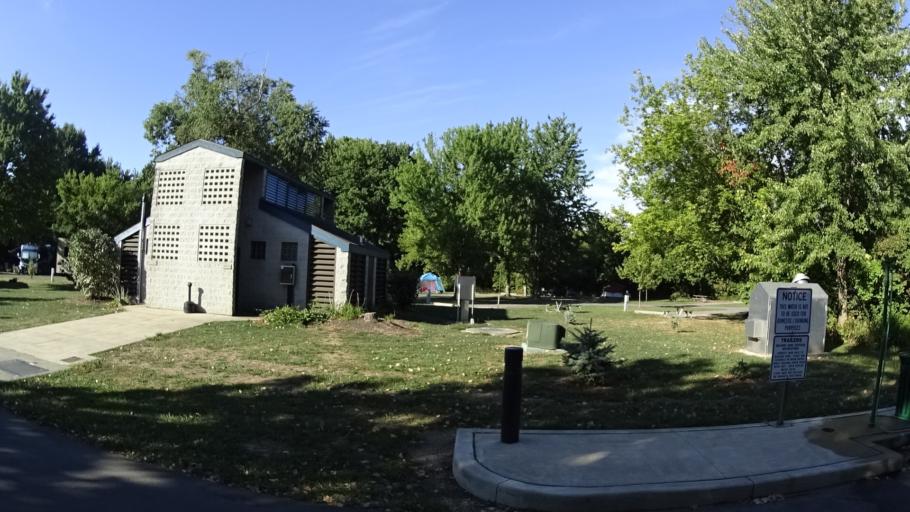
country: US
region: Ohio
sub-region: Erie County
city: Sandusky
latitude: 41.6124
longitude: -82.7043
